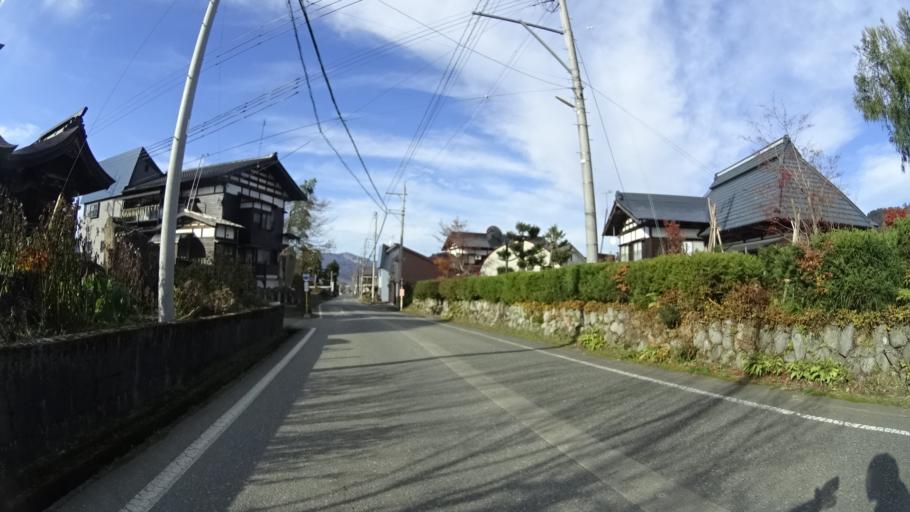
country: JP
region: Niigata
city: Shiozawa
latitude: 37.0148
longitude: 138.8797
